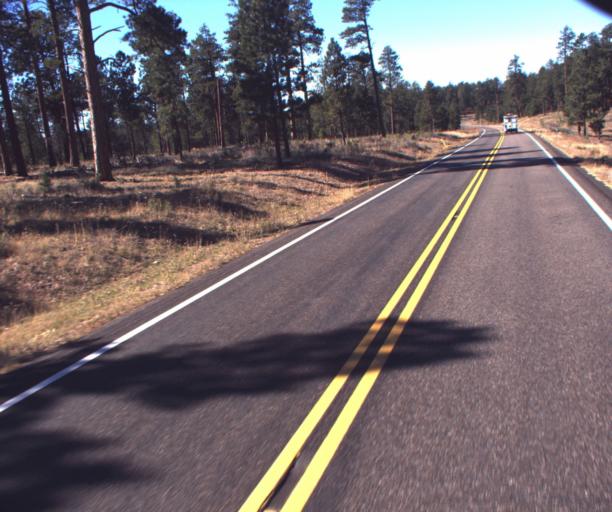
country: US
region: Arizona
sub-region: Coconino County
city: Fredonia
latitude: 36.6687
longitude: -112.2020
